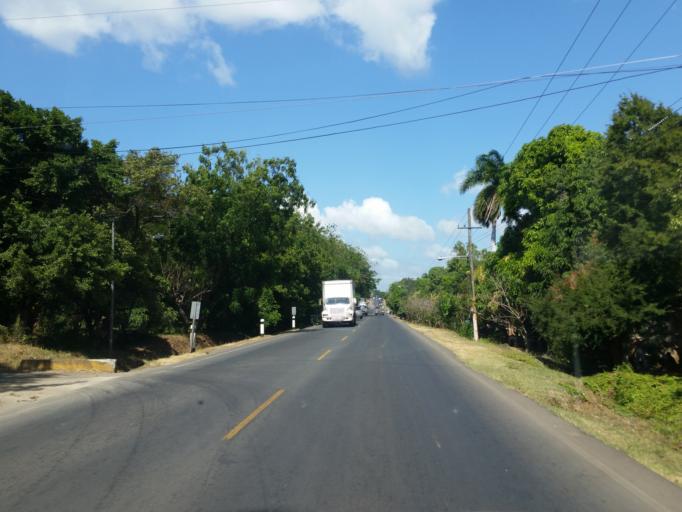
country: NI
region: Granada
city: Nandaime
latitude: 11.7710
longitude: -86.0511
